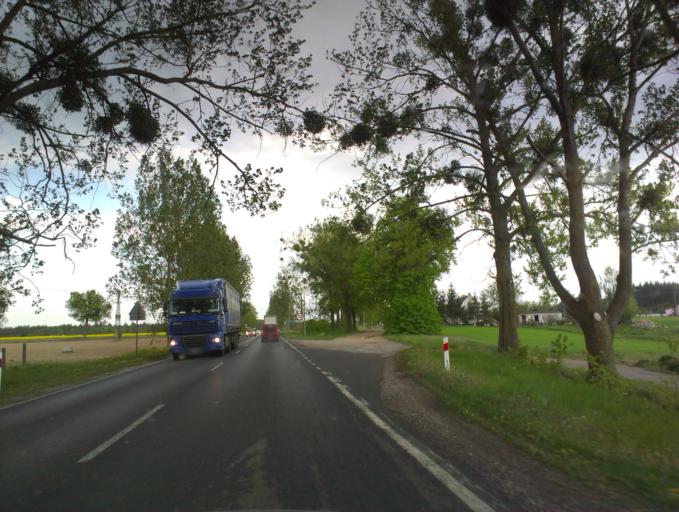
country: PL
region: Kujawsko-Pomorskie
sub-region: Powiat swiecki
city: Drzycim
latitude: 53.4206
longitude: 18.3427
